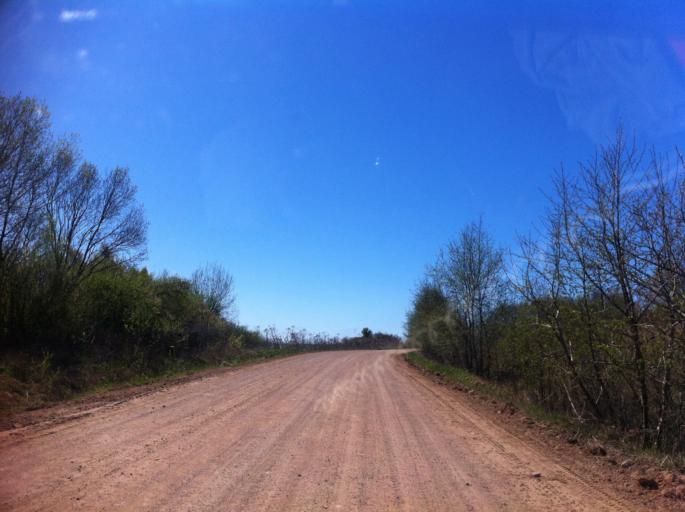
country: RU
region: Pskov
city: Izborsk
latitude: 57.8049
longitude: 27.9731
